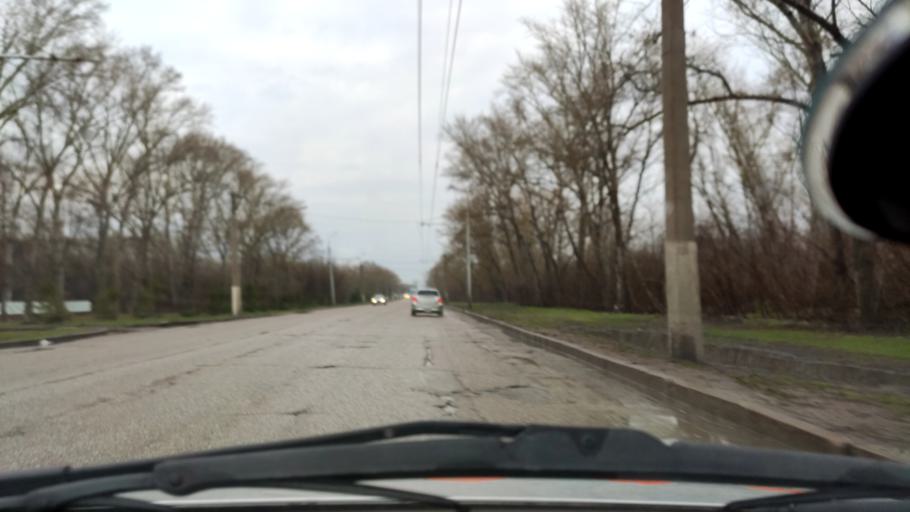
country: RU
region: Bashkortostan
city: Sterlitamak
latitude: 53.6580
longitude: 55.9488
